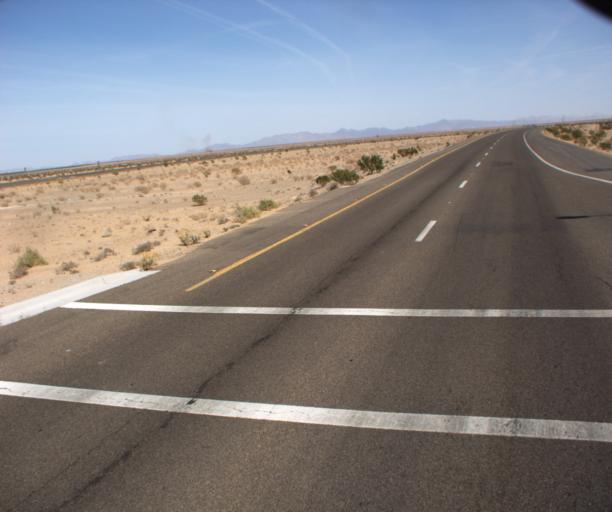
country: US
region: Arizona
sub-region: Yuma County
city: Somerton
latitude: 32.4958
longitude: -114.6480
